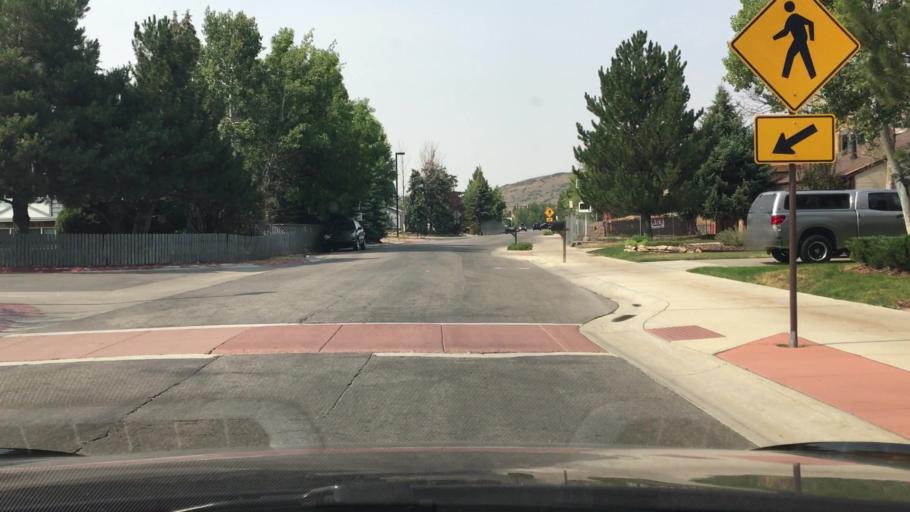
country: US
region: Utah
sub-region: Summit County
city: Park City
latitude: 40.6656
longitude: -111.4918
